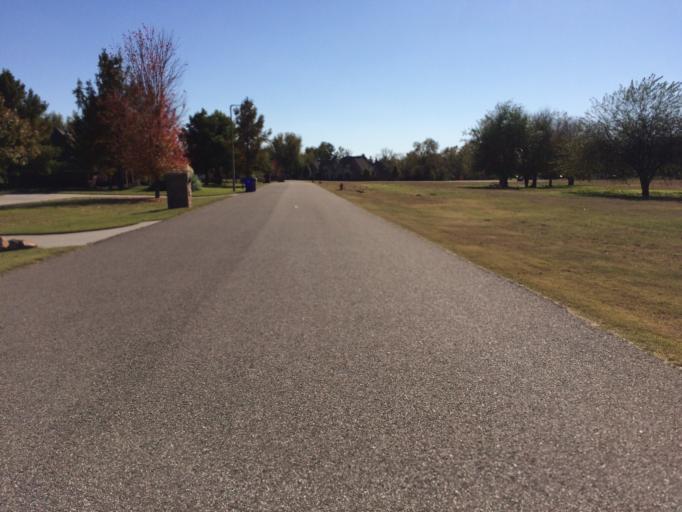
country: US
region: Oklahoma
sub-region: Cleveland County
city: Noble
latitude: 35.1638
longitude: -97.4222
